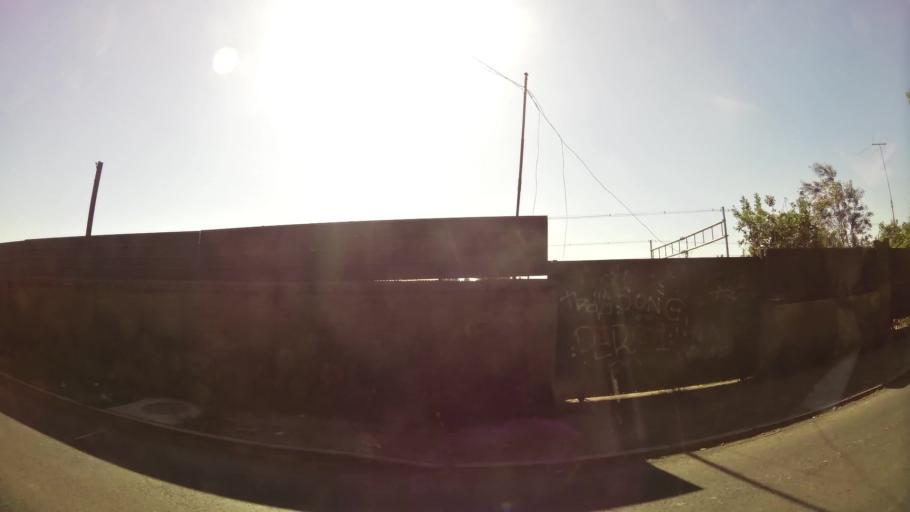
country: CL
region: Santiago Metropolitan
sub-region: Provincia de Maipo
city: San Bernardo
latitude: -33.5629
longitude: -70.6970
